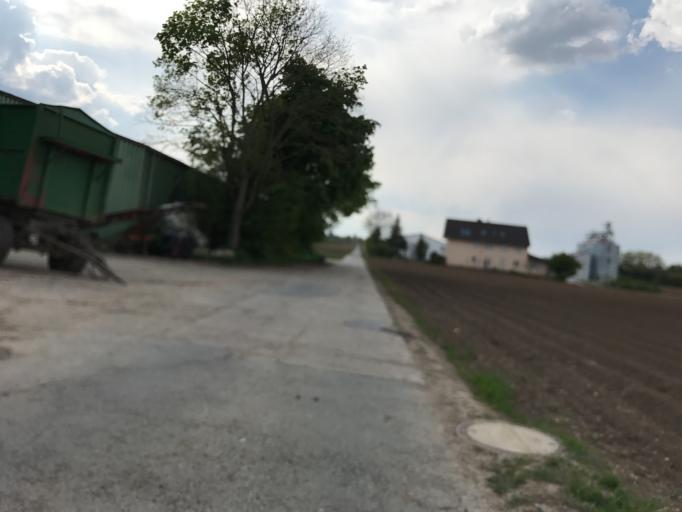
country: DE
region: Rheinland-Pfalz
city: Gau-Bischofsheim
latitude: 49.9435
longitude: 8.2714
